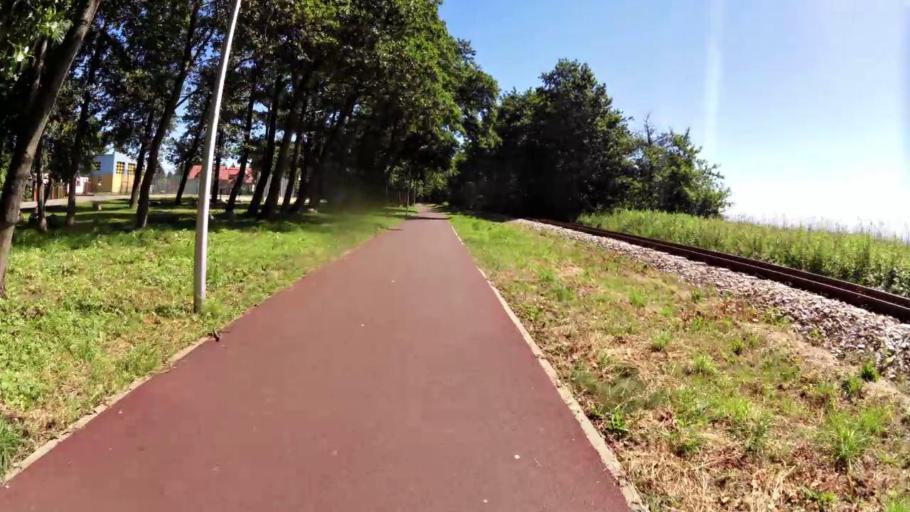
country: PL
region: West Pomeranian Voivodeship
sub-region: Powiat gryficki
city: Karnice
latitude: 54.0937
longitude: 15.0840
